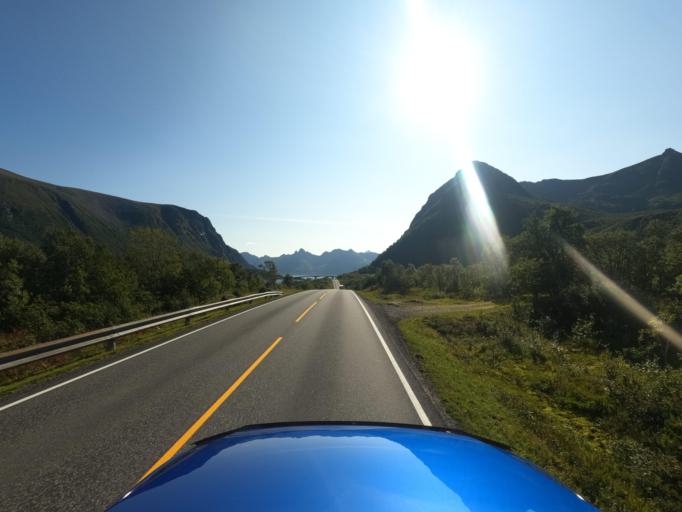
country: NO
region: Nordland
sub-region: Vagan
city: Kabelvag
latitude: 68.2767
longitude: 14.1349
